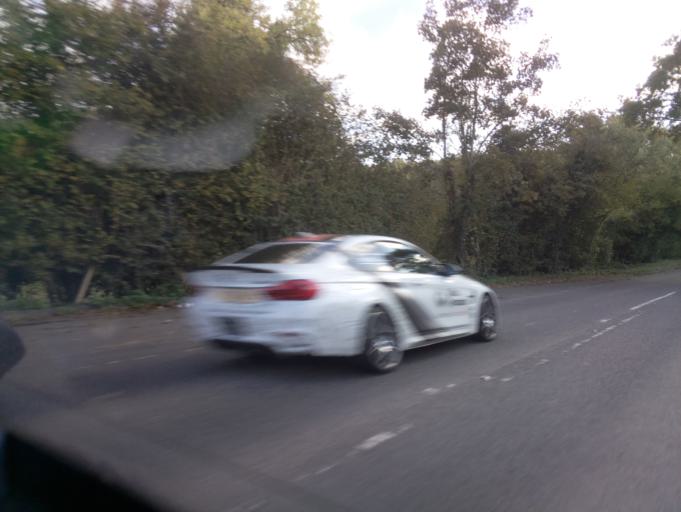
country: GB
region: England
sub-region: Herefordshire
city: Ledbury
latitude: 52.0424
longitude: -2.4113
